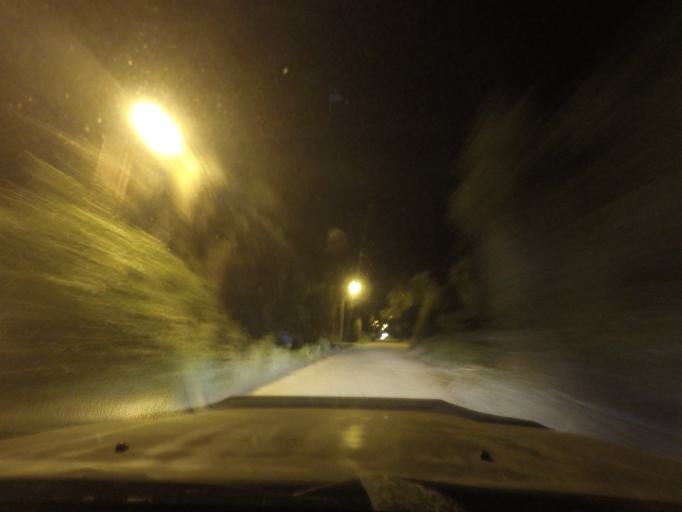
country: BO
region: Cochabamba
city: Cochabamba
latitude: -17.3731
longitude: -66.2074
